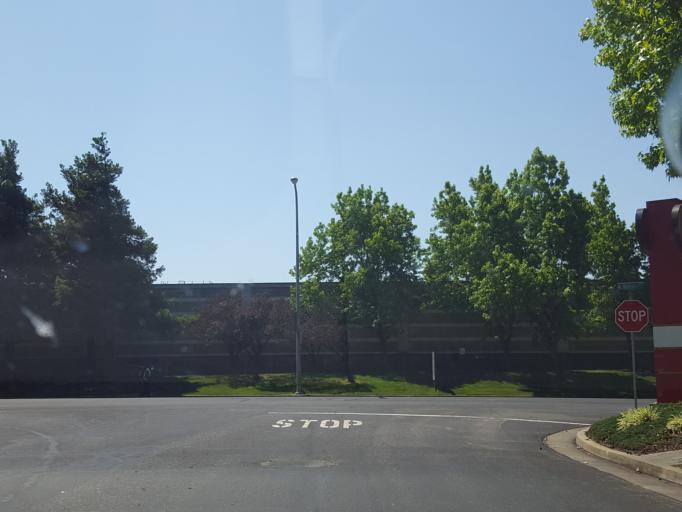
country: US
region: California
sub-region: Solano County
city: Suisun
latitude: 38.2377
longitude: -122.0780
